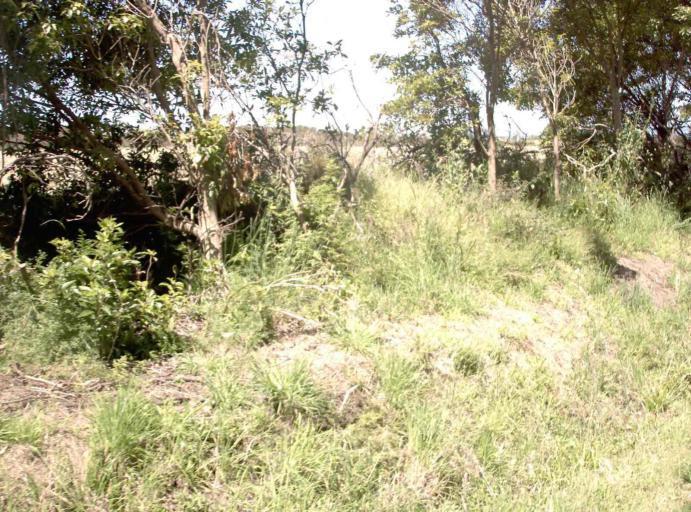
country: AU
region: Victoria
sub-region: Bass Coast
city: North Wonthaggi
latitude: -38.7780
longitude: 146.0767
